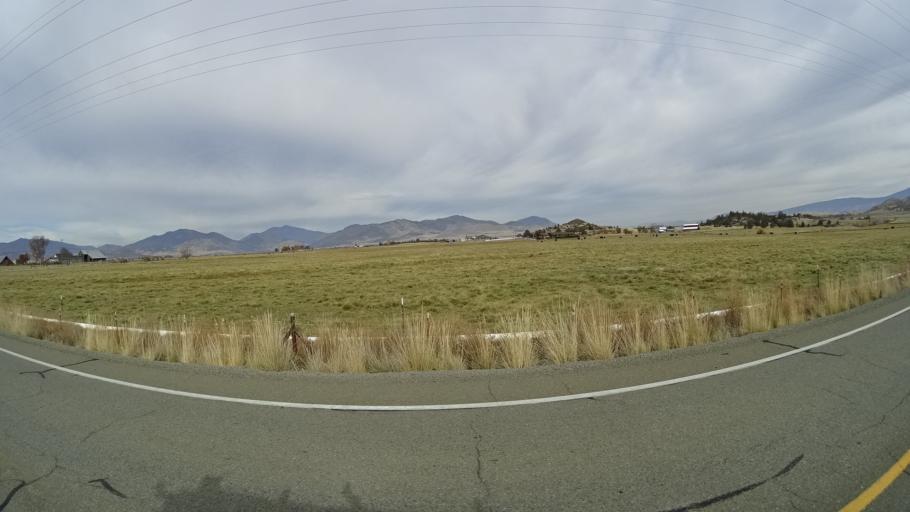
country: US
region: California
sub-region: Siskiyou County
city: Montague
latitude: 41.7058
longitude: -122.5479
